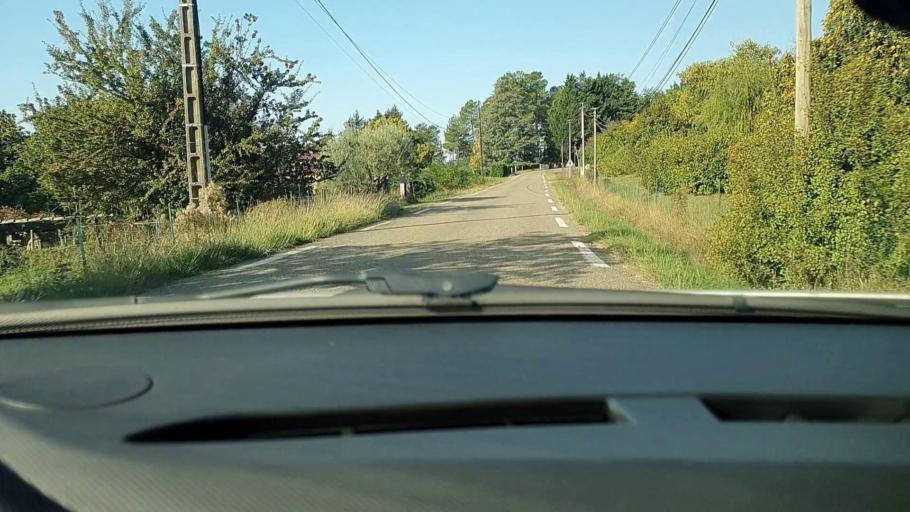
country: FR
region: Languedoc-Roussillon
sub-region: Departement du Gard
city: Besseges
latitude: 44.3047
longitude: 4.0873
